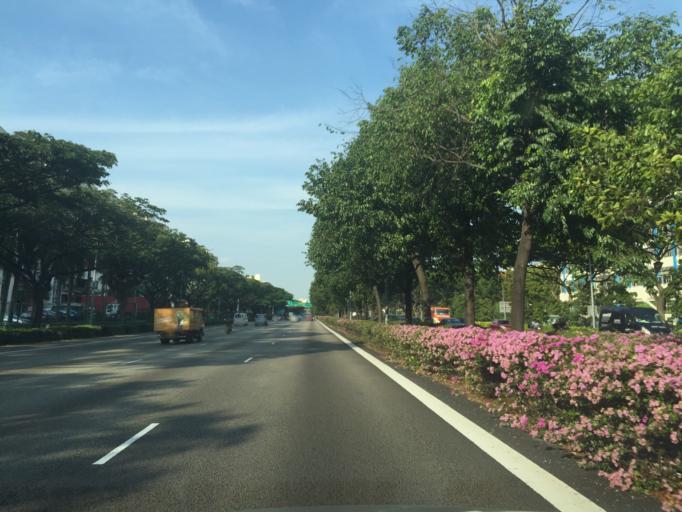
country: SG
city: Singapore
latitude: 1.3239
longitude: 103.8951
